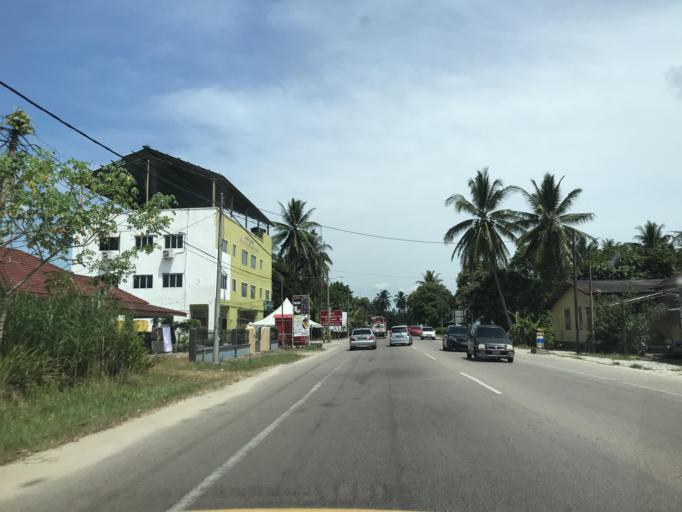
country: MY
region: Kelantan
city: Kota Bharu
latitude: 6.1197
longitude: 102.1898
